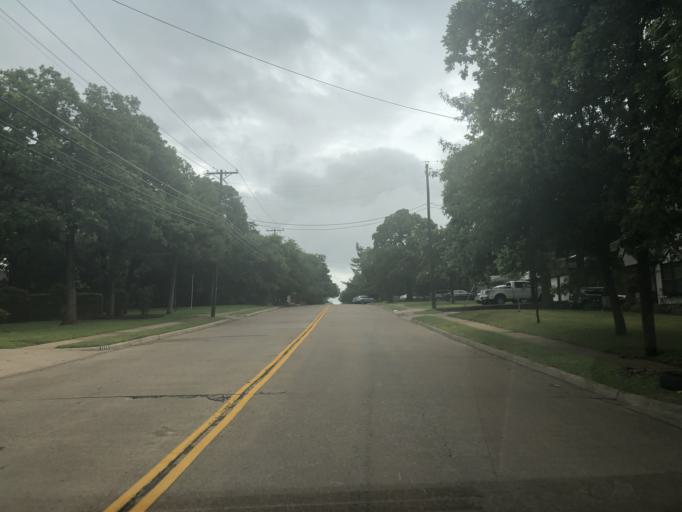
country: US
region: Texas
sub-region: Dallas County
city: Irving
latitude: 32.7997
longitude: -96.9469
